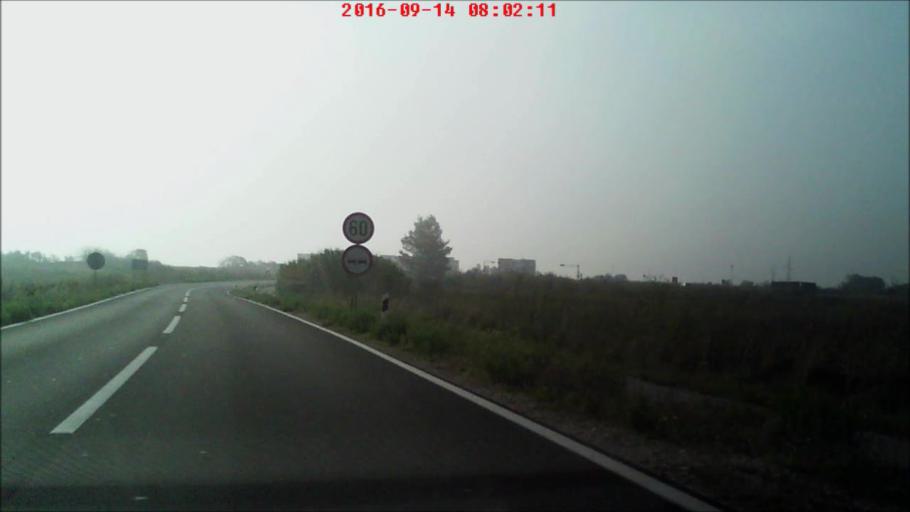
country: HR
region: Zadarska
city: Nin
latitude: 44.2473
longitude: 15.1654
